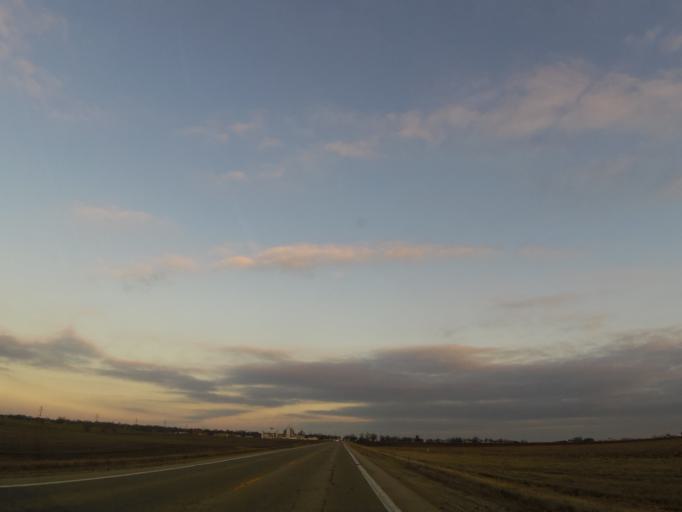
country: US
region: Illinois
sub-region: McLean County
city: Gridley
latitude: 40.7393
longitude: -88.9041
